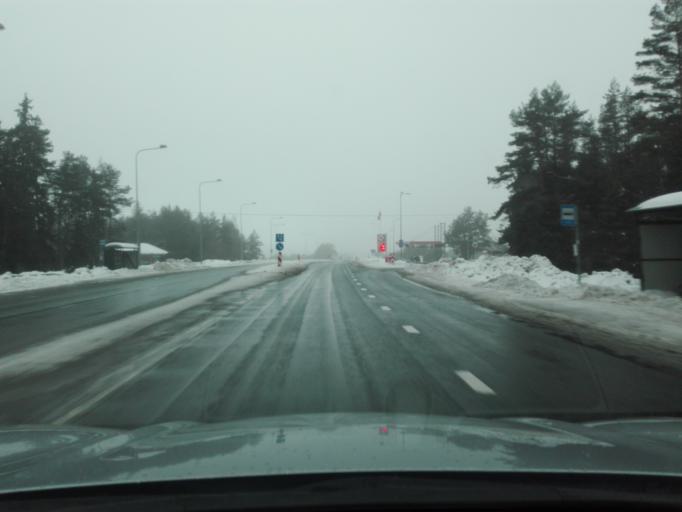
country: EE
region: Raplamaa
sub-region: Kohila vald
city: Kohila
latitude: 59.1827
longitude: 24.7832
